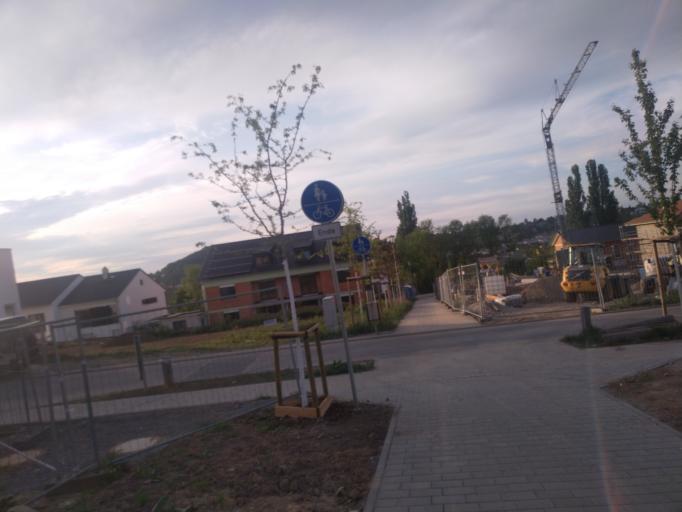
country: DE
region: Baden-Wuerttemberg
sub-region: Karlsruhe Region
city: Pforzheim
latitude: 48.8843
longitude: 8.6783
